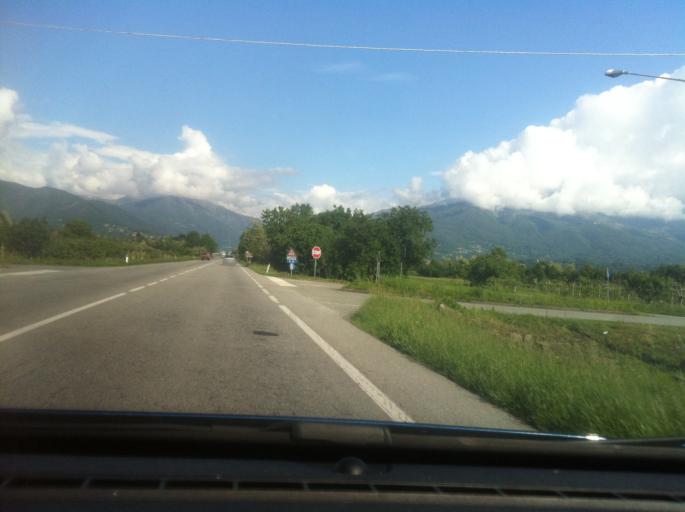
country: IT
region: Piedmont
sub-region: Provincia di Torino
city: Salassa
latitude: 45.3612
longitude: 7.6900
